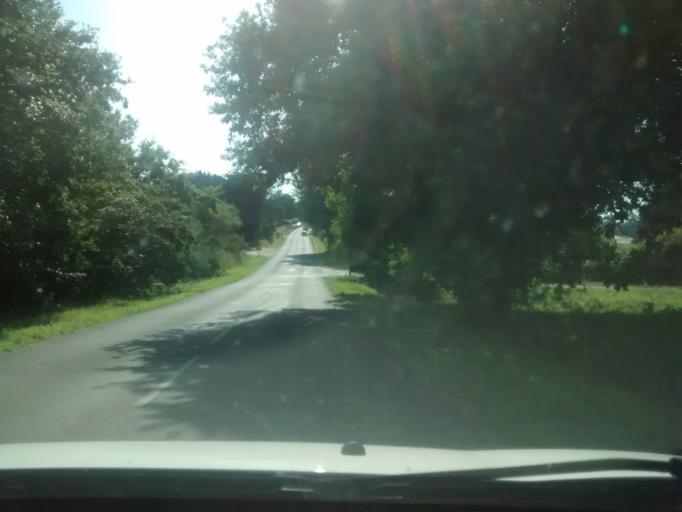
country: FR
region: Brittany
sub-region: Departement d'Ille-et-Vilaine
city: Saint-Coulomb
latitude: 48.6816
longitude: -1.9510
